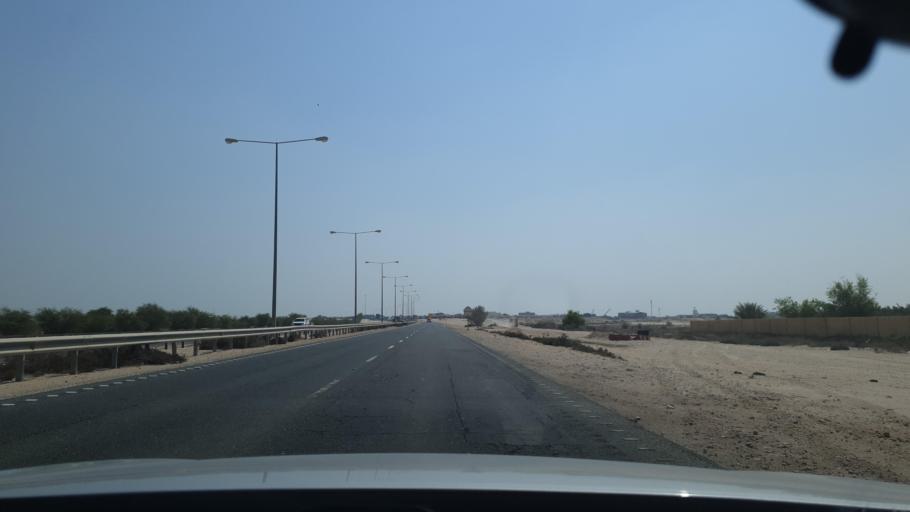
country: QA
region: Al Khawr
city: Al Khawr
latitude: 25.7283
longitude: 51.4955
